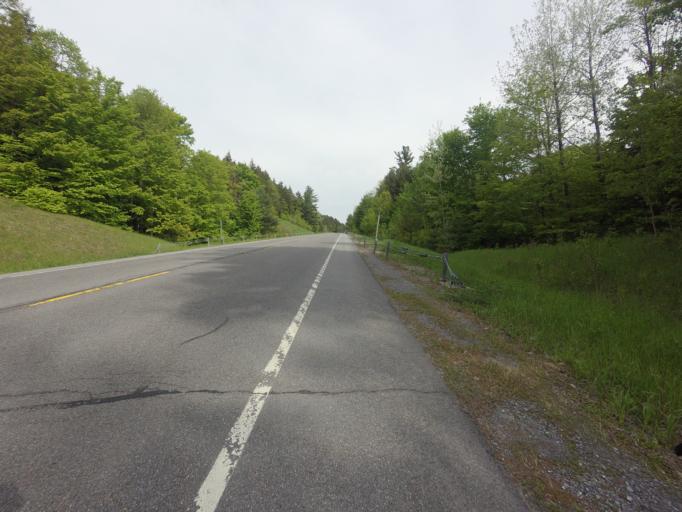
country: US
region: New York
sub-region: St. Lawrence County
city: Gouverneur
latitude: 44.2871
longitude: -75.2109
